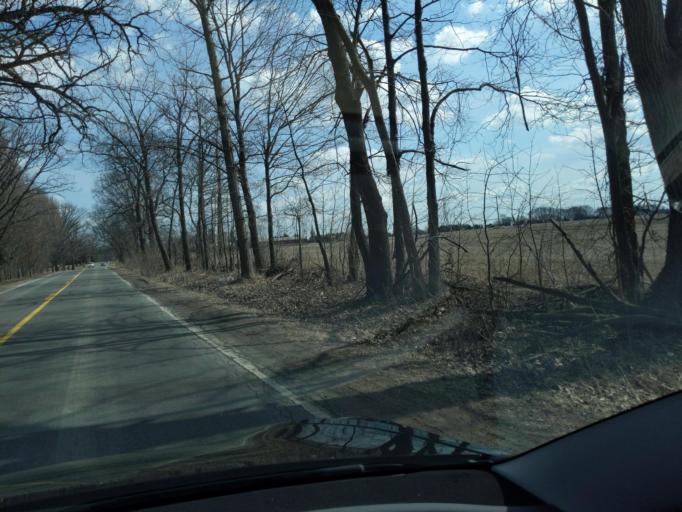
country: US
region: Michigan
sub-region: Washtenaw County
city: Dexter
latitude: 42.3842
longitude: -83.8854
